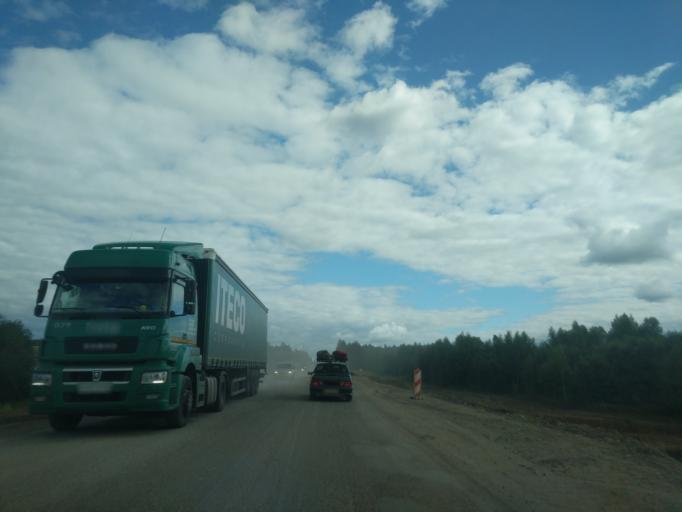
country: RU
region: Kostroma
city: Sudislavl'
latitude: 57.8732
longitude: 41.7391
